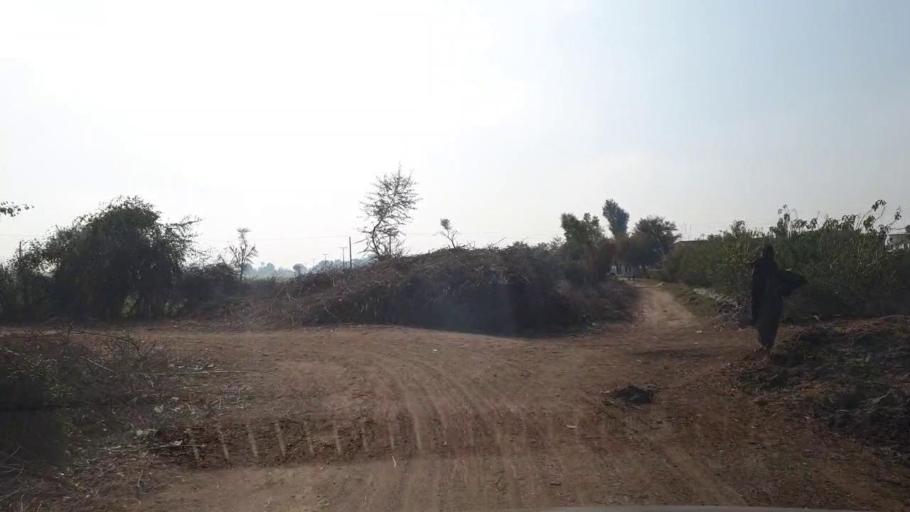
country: PK
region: Sindh
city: Shahdadpur
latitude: 26.0050
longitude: 68.5906
